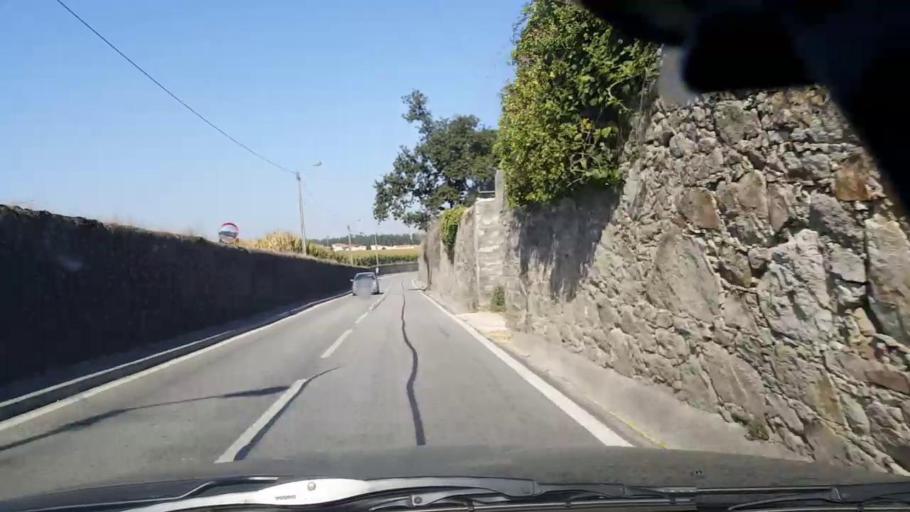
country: PT
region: Porto
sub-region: Vila do Conde
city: Arvore
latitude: 41.3769
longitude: -8.6755
